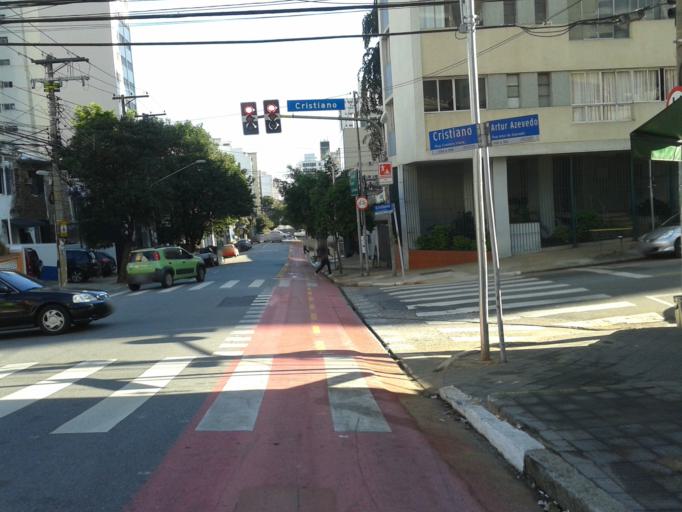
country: BR
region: Sao Paulo
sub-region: Sao Paulo
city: Sao Paulo
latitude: -23.5596
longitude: -46.6767
